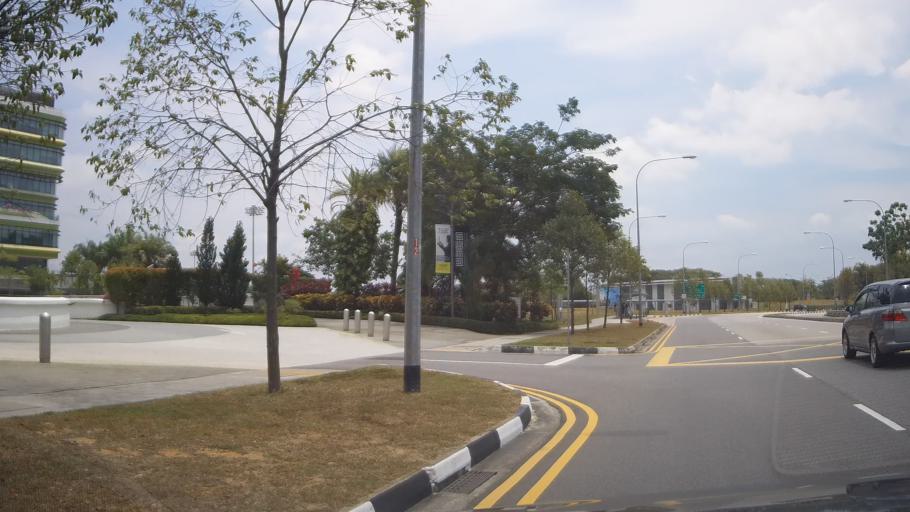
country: SG
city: Singapore
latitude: 1.3397
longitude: 103.9630
